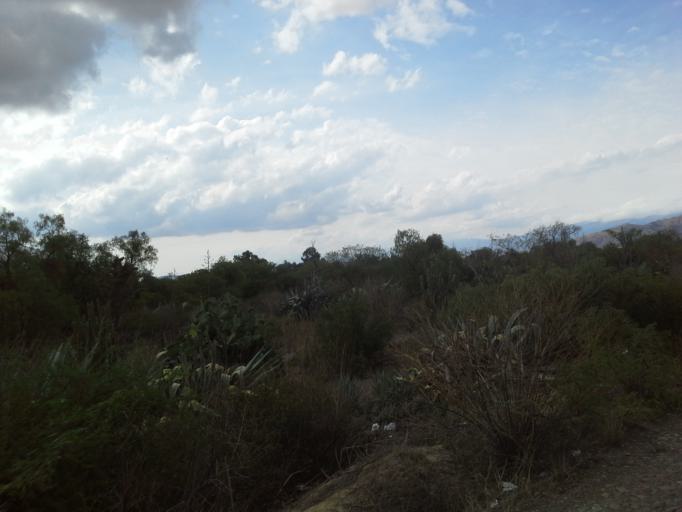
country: BO
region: Cochabamba
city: Tarata
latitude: -17.6066
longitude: -66.0219
